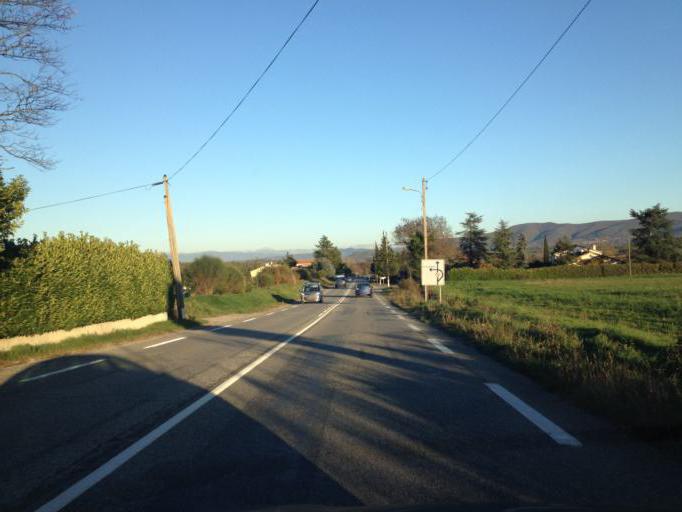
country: FR
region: Rhone-Alpes
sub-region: Departement de l'Ardeche
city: Chomerac
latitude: 44.7087
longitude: 4.6715
